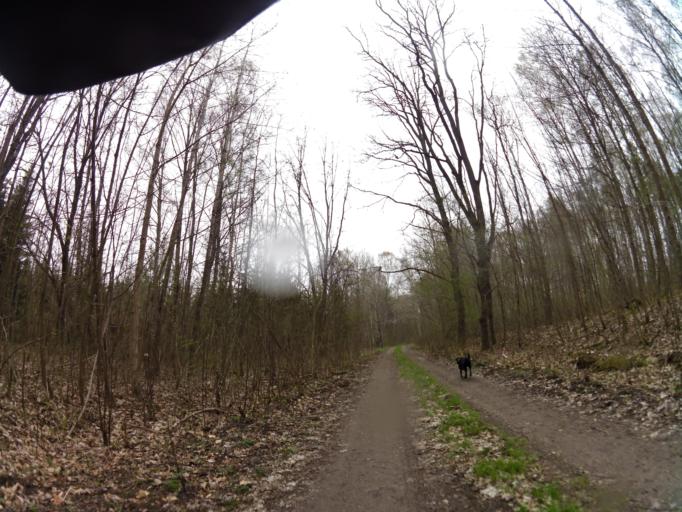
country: PL
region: West Pomeranian Voivodeship
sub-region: Powiat koszalinski
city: Bobolice
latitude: 53.9851
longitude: 16.6496
